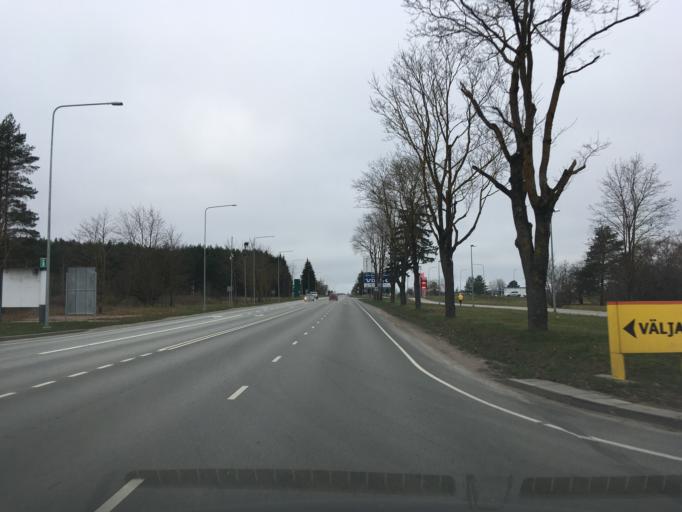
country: EE
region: Ida-Virumaa
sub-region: Narva linn
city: Narva
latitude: 59.3847
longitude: 28.1572
